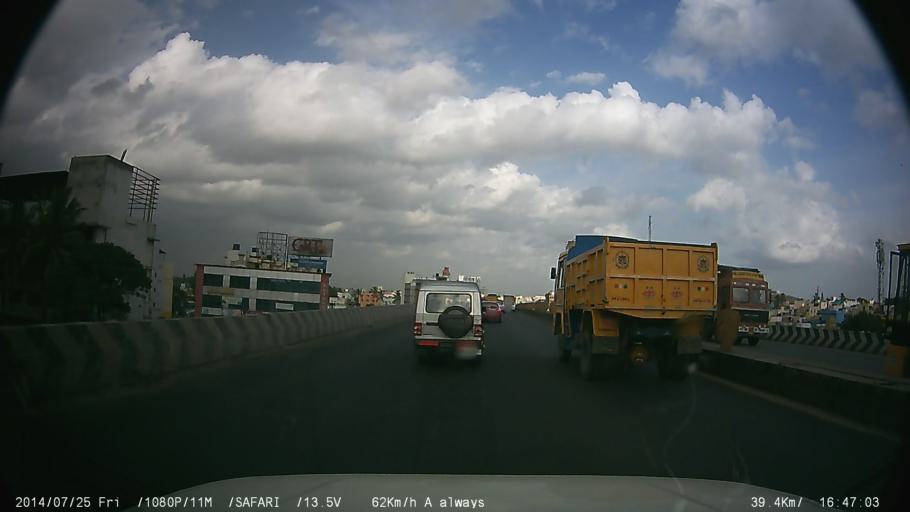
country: IN
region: Tamil Nadu
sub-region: Krishnagiri
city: Hosur
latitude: 12.7354
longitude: 77.8288
